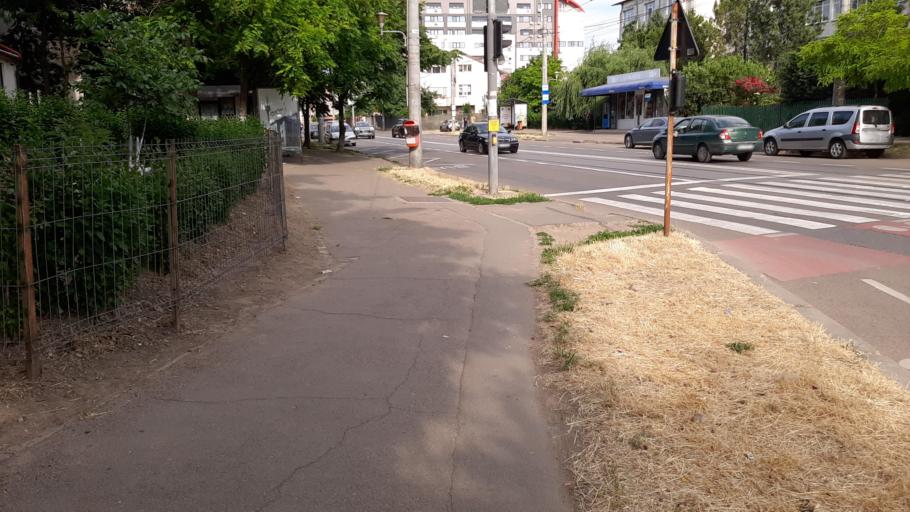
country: RO
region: Galati
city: Galati
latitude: 45.4407
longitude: 28.0294
